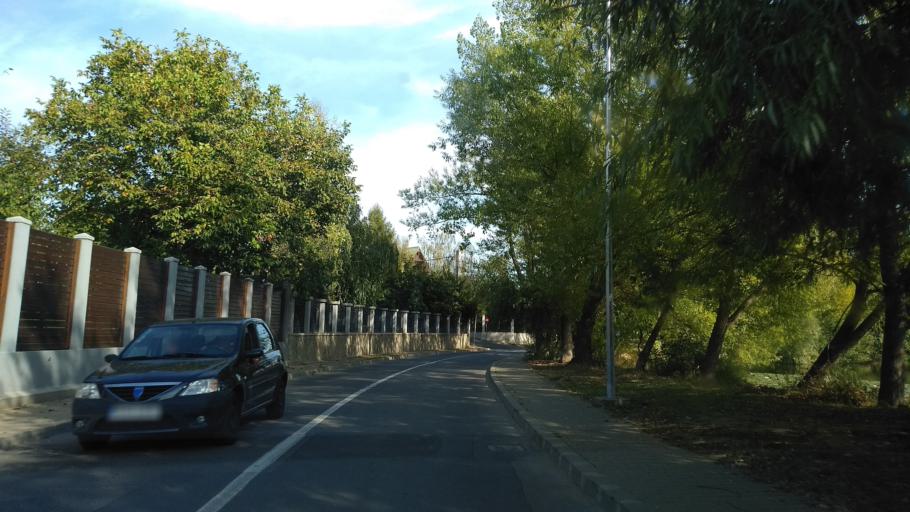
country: RO
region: Ilfov
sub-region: Comuna Chitila
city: Chitila
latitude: 44.5122
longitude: 25.9889
